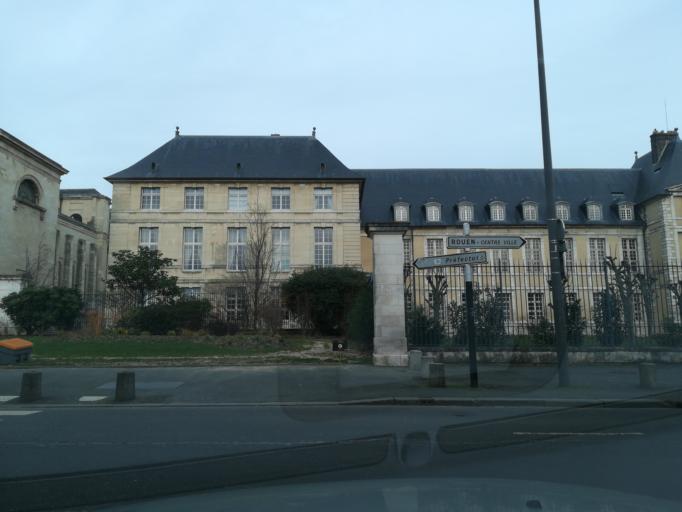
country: FR
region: Haute-Normandie
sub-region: Departement de la Seine-Maritime
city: Rouen
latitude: 49.4451
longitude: 1.0804
